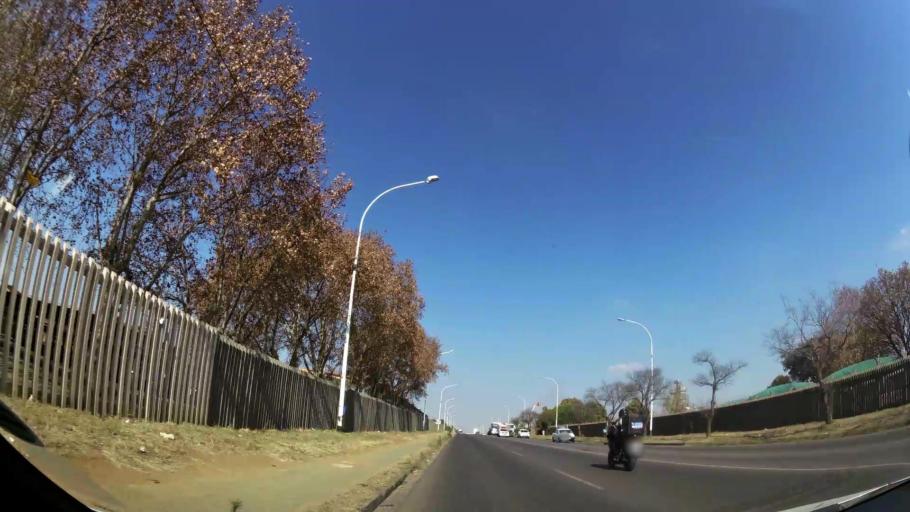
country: ZA
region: Gauteng
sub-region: Ekurhuleni Metropolitan Municipality
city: Boksburg
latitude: -26.2206
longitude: 28.2900
